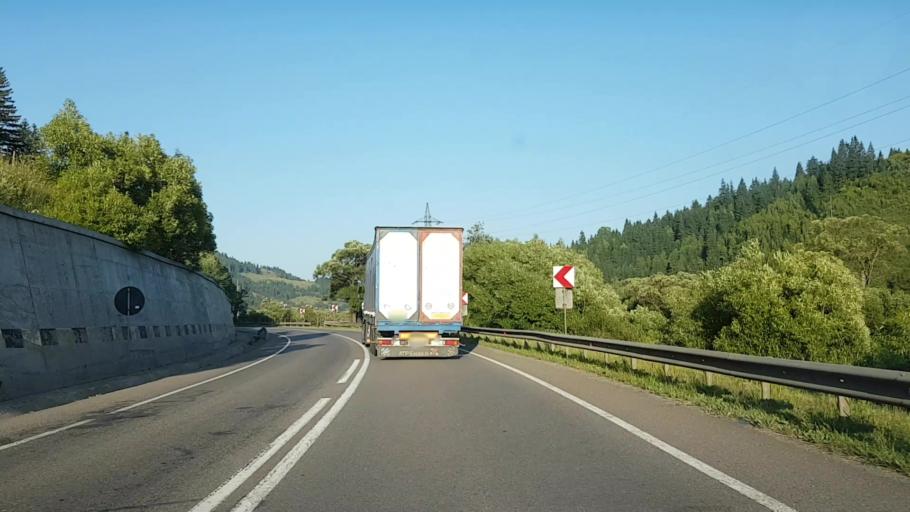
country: RO
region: Suceava
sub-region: Comuna Dorna Candrenilor
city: Dorna Candrenilor
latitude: 47.3555
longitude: 25.2829
